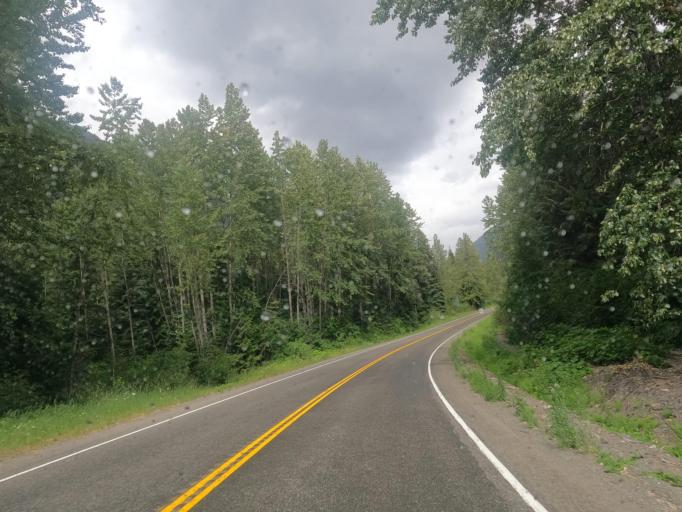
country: CA
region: British Columbia
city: Lillooet
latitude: 50.4725
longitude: -122.2323
